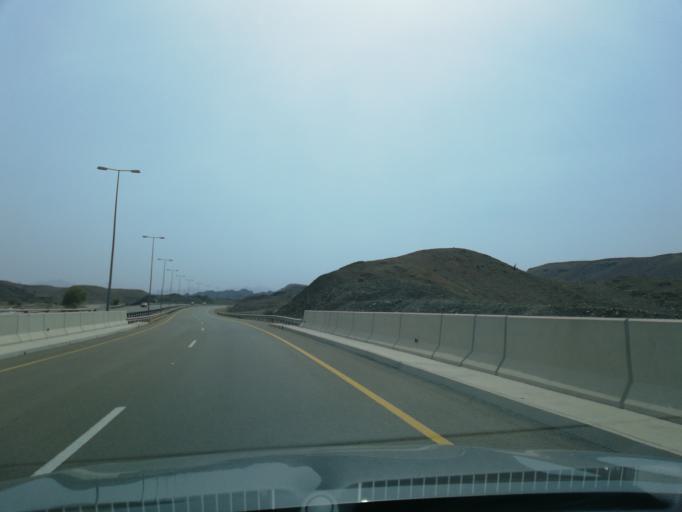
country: OM
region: Al Batinah
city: Al Liwa'
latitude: 24.3200
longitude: 56.4645
